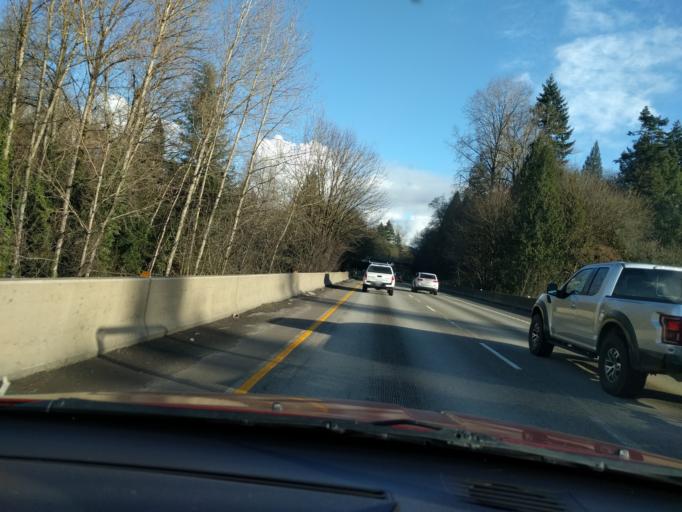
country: US
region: Oregon
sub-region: Clackamas County
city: Stafford
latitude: 45.3663
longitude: -122.6873
